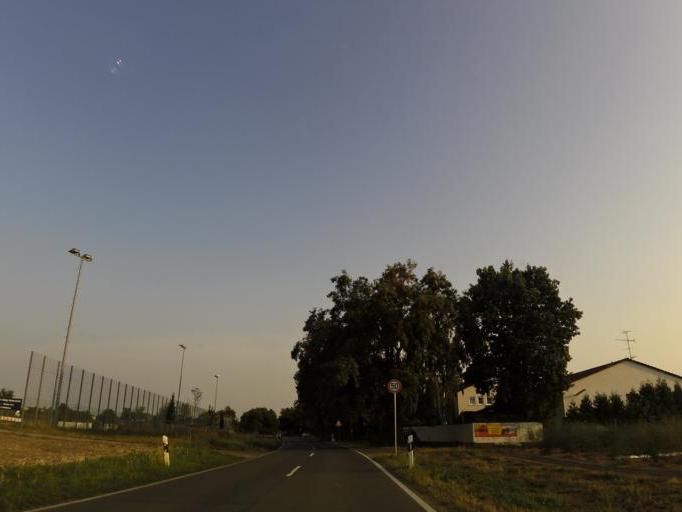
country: DE
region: Hesse
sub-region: Regierungsbezirk Darmstadt
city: Buttelborn
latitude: 49.9343
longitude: 8.5434
